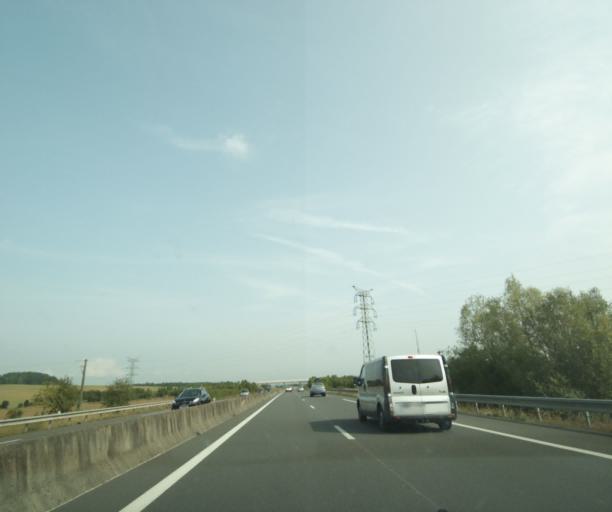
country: FR
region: Pays de la Loire
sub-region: Departement de la Sarthe
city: Arconnay
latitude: 48.3763
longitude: 0.1034
